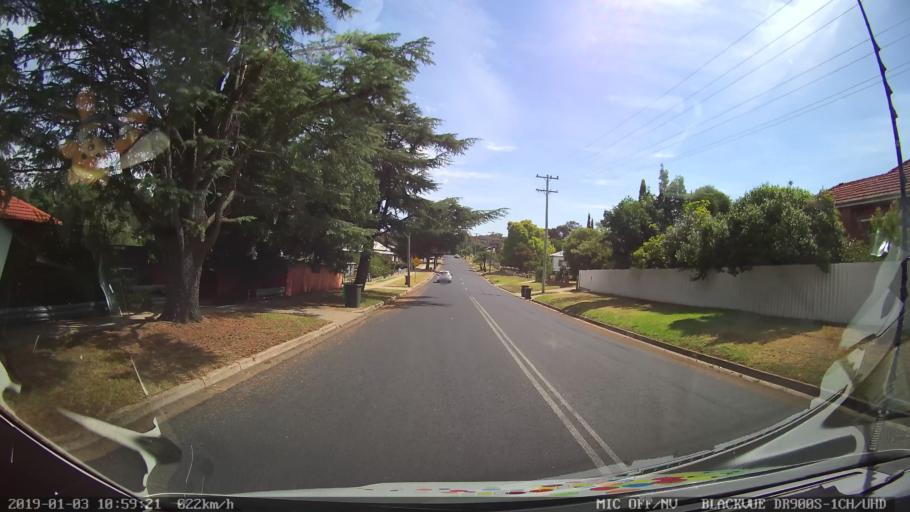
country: AU
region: New South Wales
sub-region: Young
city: Young
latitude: -34.3081
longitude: 148.2988
